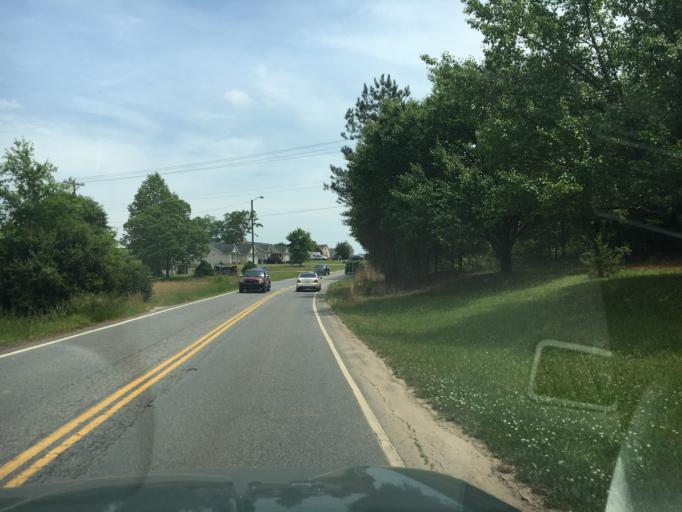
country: US
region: South Carolina
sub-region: Spartanburg County
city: Wellford
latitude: 34.9948
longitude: -82.1083
